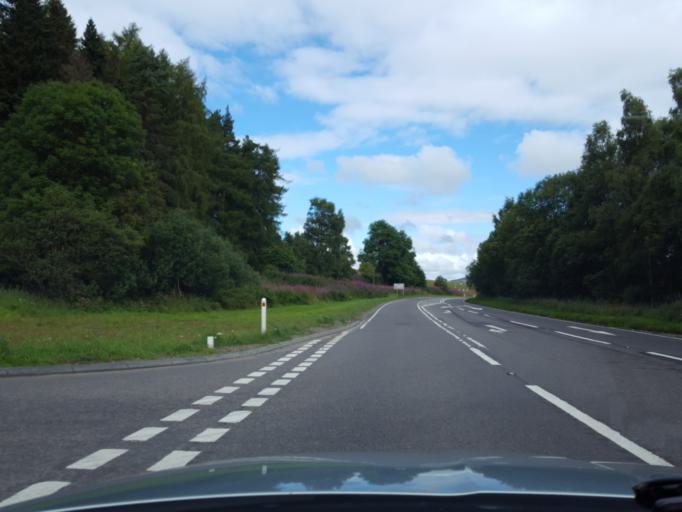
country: GB
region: Scotland
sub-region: Moray
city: Rothes
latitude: 57.4983
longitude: -3.1914
